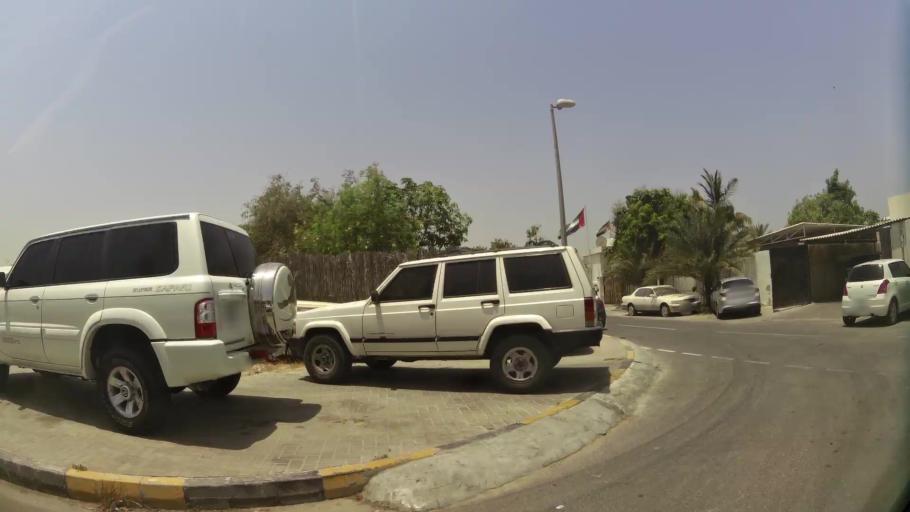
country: AE
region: Ash Shariqah
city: Sharjah
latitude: 25.3420
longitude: 55.3679
